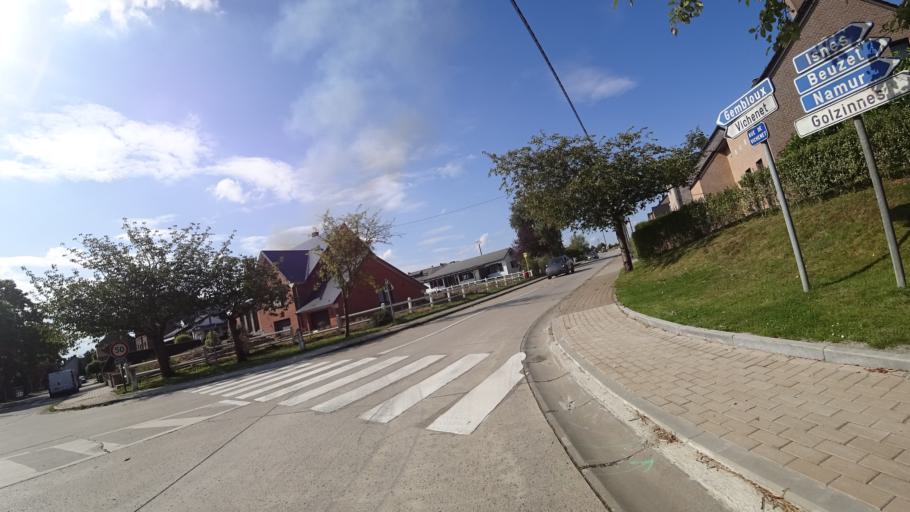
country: BE
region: Wallonia
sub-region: Province de Namur
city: Gembloux
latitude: 50.5195
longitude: 4.7013
